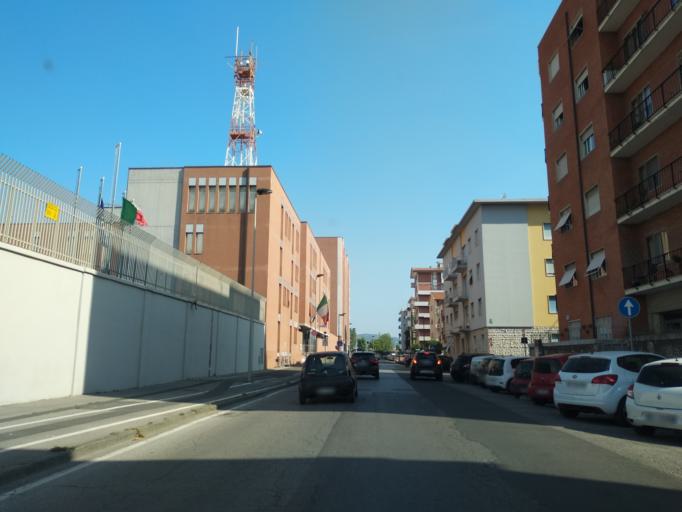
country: IT
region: Tuscany
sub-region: Provincia di Livorno
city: Livorno
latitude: 43.5398
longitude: 10.3214
